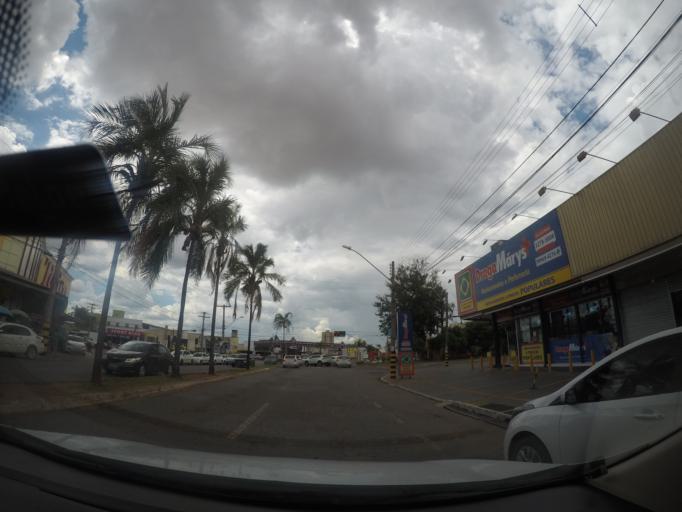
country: BR
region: Goias
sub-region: Goiania
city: Goiania
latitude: -16.6971
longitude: -49.2845
